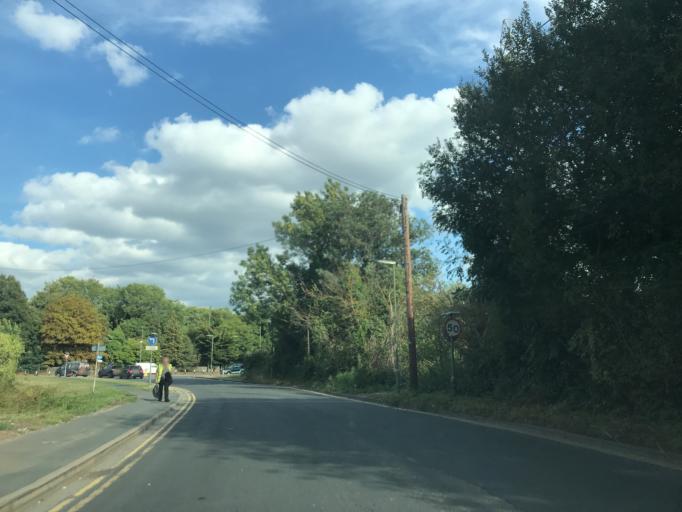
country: GB
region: England
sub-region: Surrey
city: Staines
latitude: 51.4598
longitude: -0.4955
